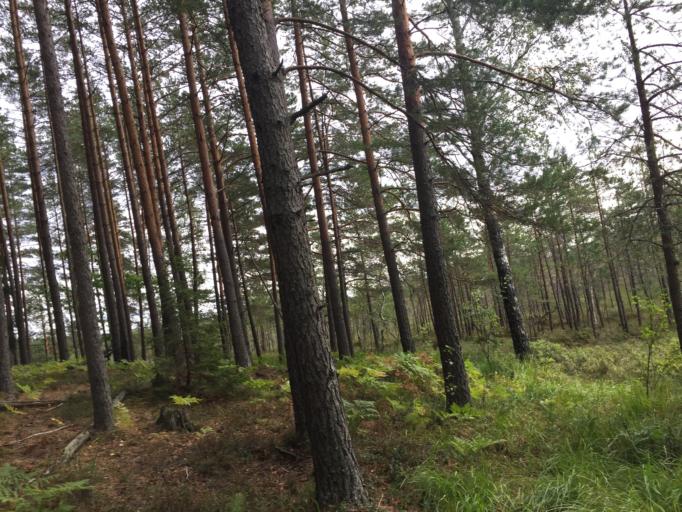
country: LV
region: Pargaujas
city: Stalbe
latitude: 57.3171
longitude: 25.0521
